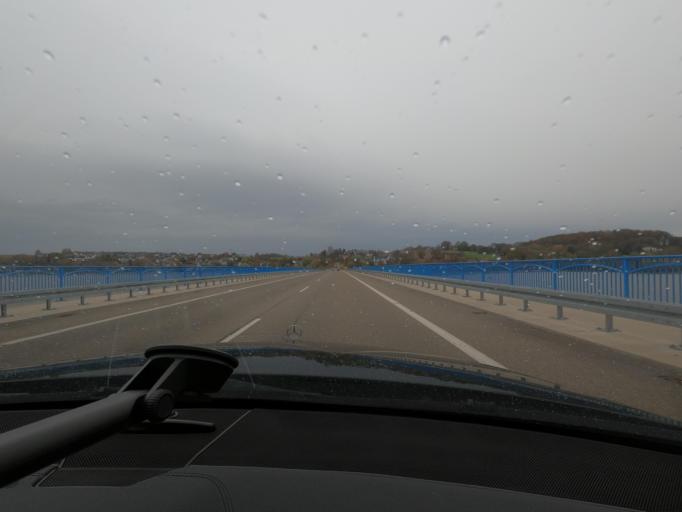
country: DE
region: North Rhine-Westphalia
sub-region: Regierungsbezirk Arnsberg
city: Mohnesee
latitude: 51.4851
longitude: 8.0878
